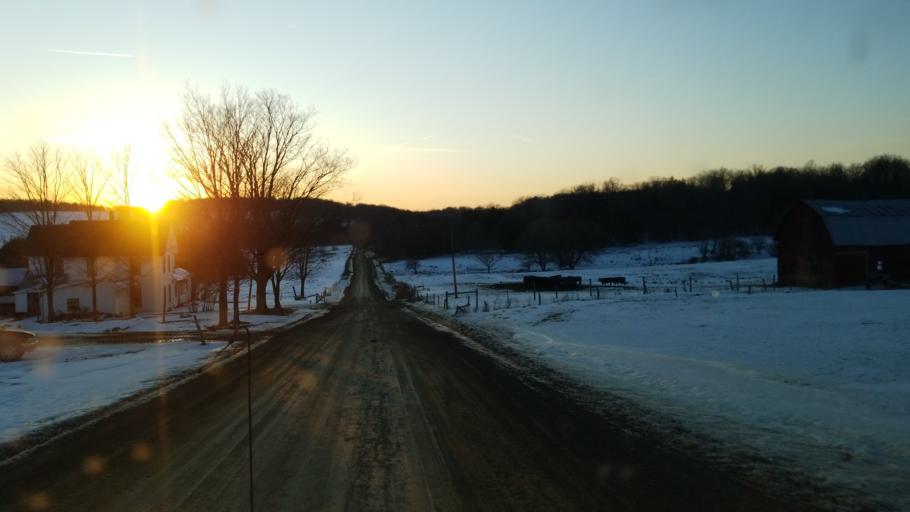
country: US
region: Pennsylvania
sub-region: Tioga County
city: Westfield
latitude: 42.0129
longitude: -77.6756
